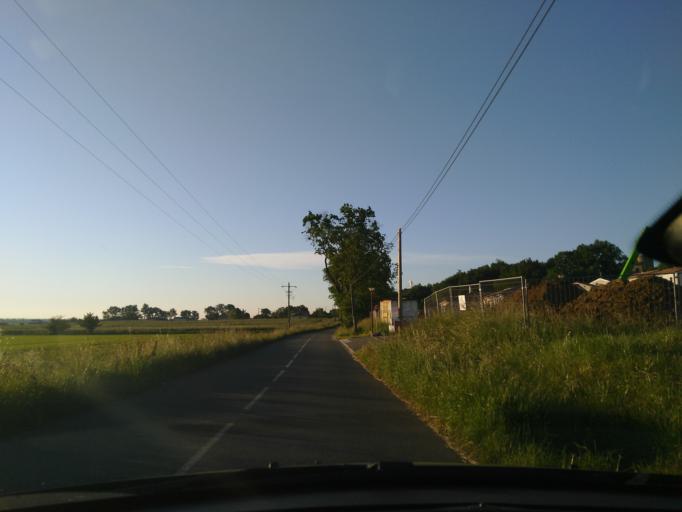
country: FR
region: Midi-Pyrenees
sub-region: Departement de la Haute-Garonne
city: Merville
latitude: 43.7298
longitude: 1.2935
